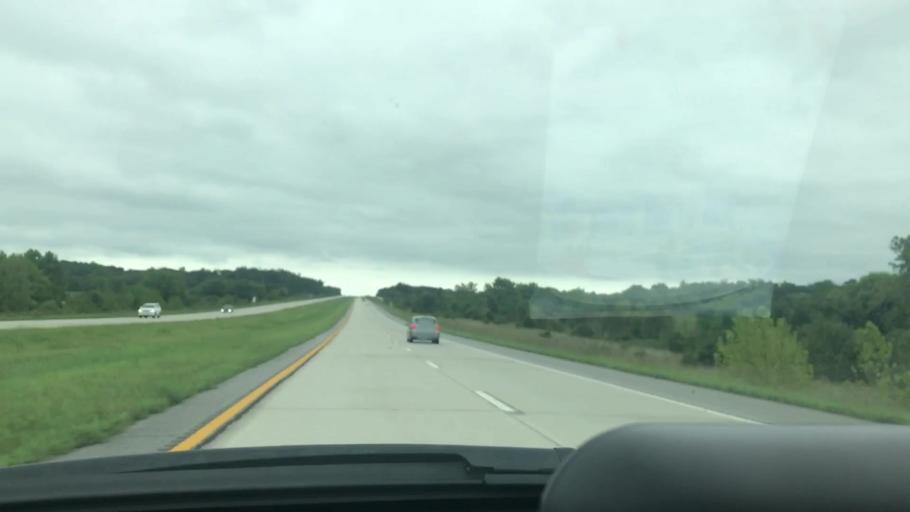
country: US
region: Missouri
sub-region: Greene County
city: Fair Grove
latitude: 37.4660
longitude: -93.1393
